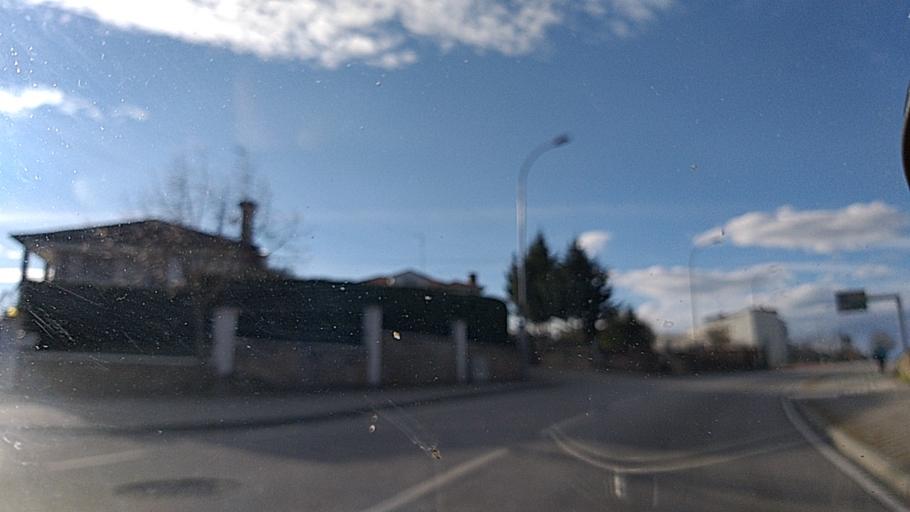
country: ES
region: Castille and Leon
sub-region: Provincia de Salamanca
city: Fuentes de Onoro
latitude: 40.6159
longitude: -6.8400
